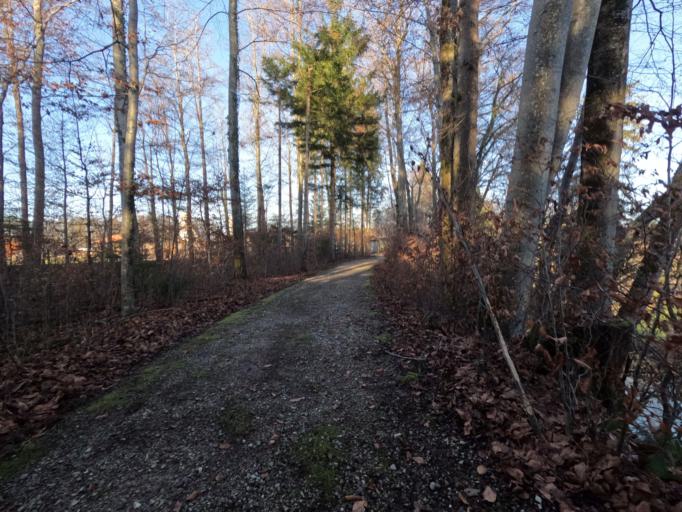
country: DE
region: Bavaria
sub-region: Upper Bavaria
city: Nussdorf
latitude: 47.8999
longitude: 12.6252
